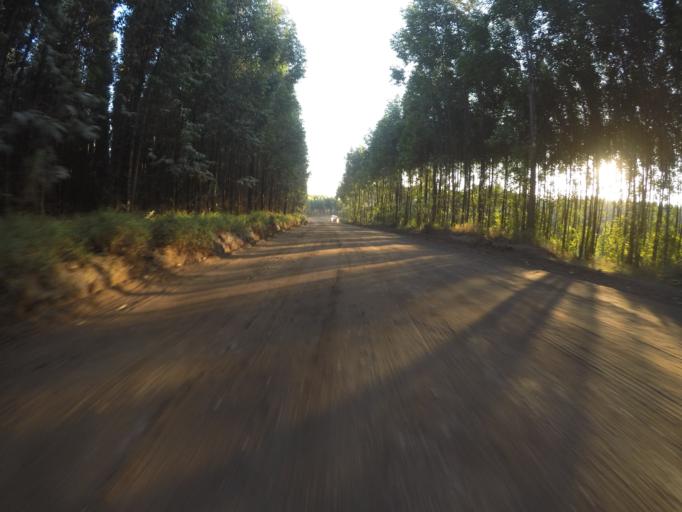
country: ZA
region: KwaZulu-Natal
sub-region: uThungulu District Municipality
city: KwaMbonambi
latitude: -28.6733
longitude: 32.1084
